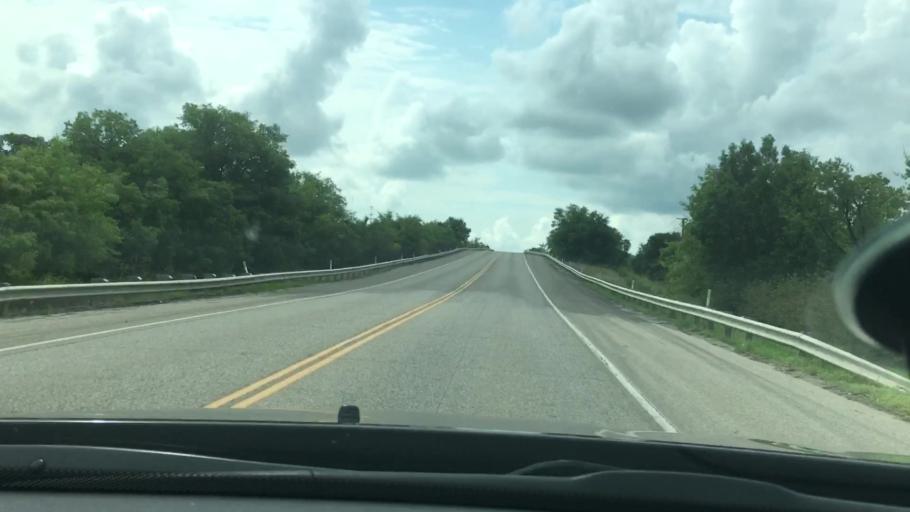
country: US
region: Oklahoma
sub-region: Carter County
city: Ardmore
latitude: 34.1951
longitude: -97.1082
